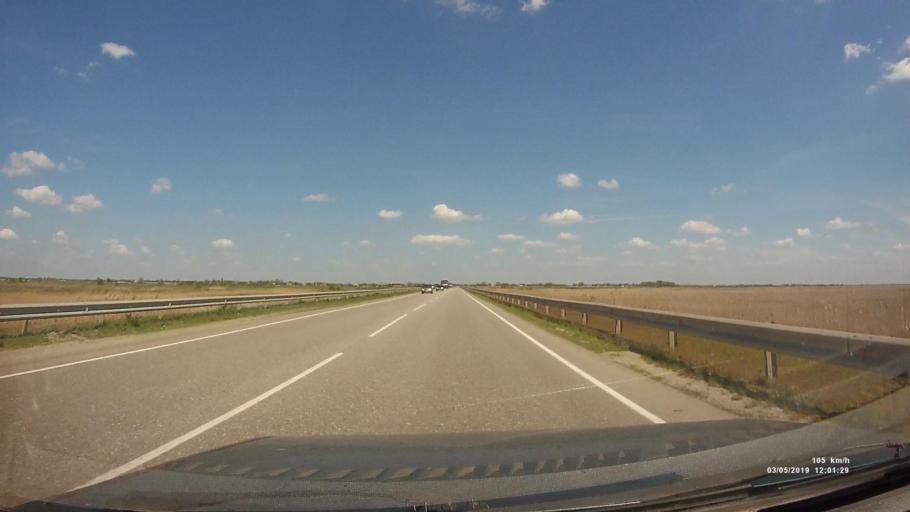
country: RU
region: Rostov
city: Bagayevskaya
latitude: 47.2636
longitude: 40.3510
